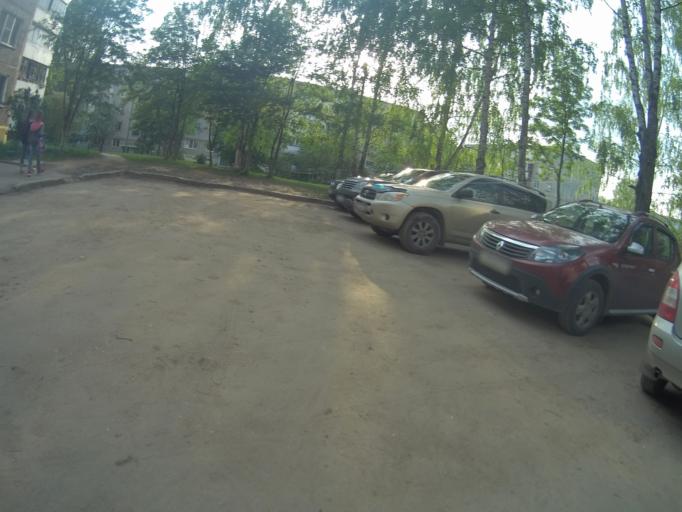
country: RU
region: Vladimir
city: Kommunar
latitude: 56.1666
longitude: 40.4437
